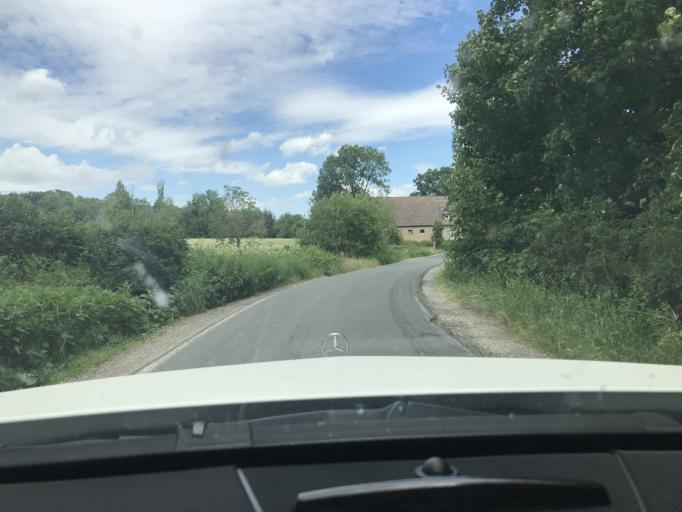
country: DE
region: Thuringia
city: Holzsussra
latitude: 51.2976
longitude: 10.6482
